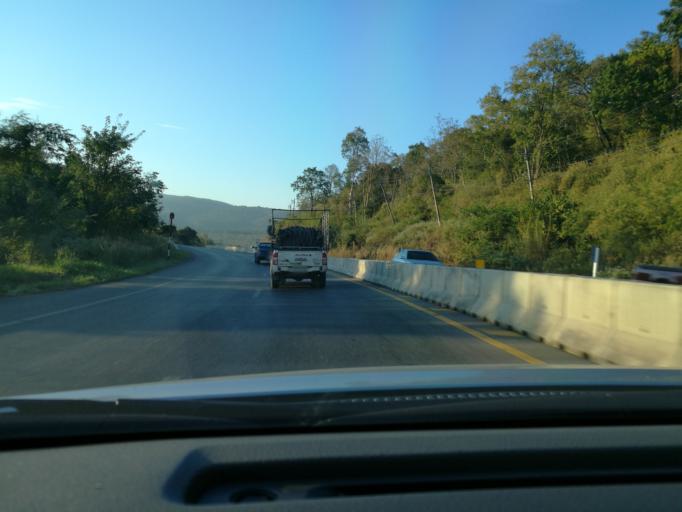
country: TH
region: Phitsanulok
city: Wang Thong
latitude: 16.8573
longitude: 100.5060
